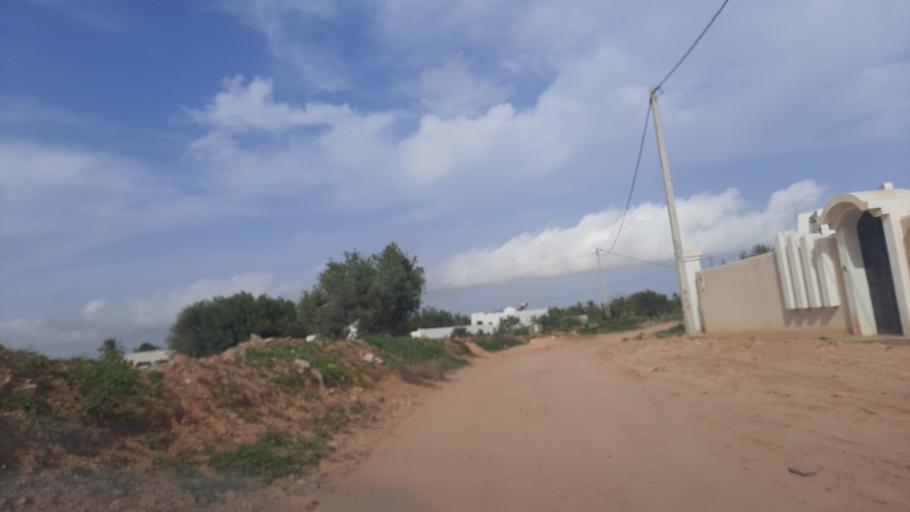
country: TN
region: Madanin
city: Midoun
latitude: 33.8048
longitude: 11.0250
